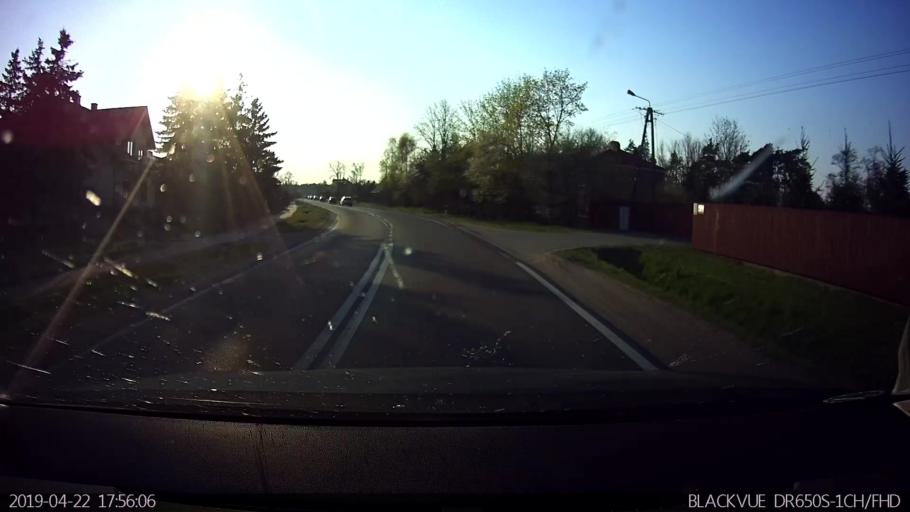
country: PL
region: Masovian Voivodeship
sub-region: Powiat wegrowski
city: Korytnica
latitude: 52.4643
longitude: 21.9117
